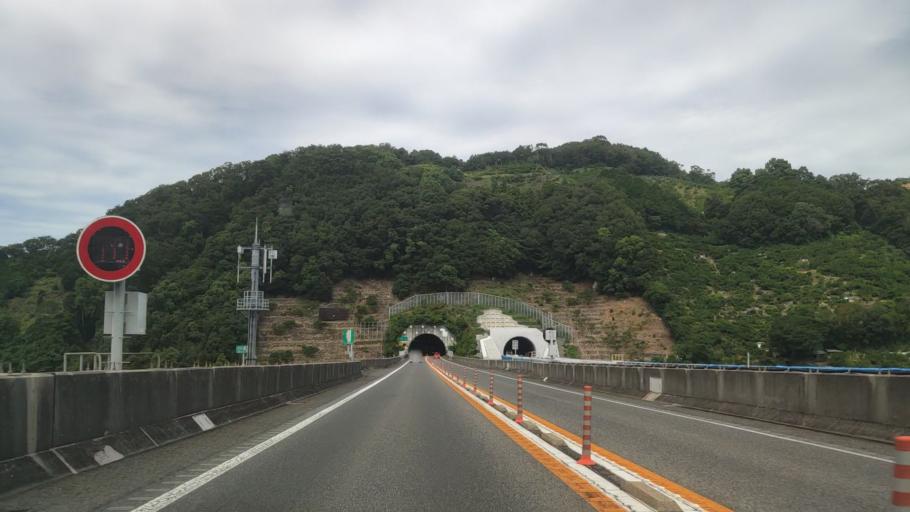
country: JP
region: Wakayama
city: Gobo
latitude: 33.9975
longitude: 135.1966
